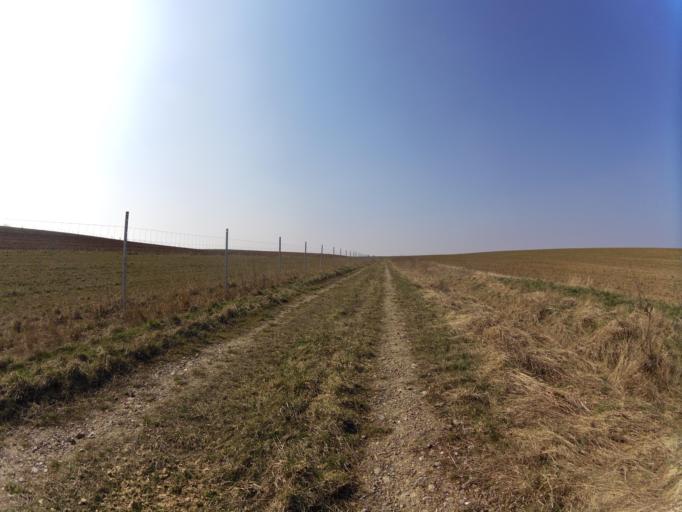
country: DE
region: Bavaria
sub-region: Regierungsbezirk Unterfranken
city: Winterhausen
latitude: 49.6757
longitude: 9.9876
